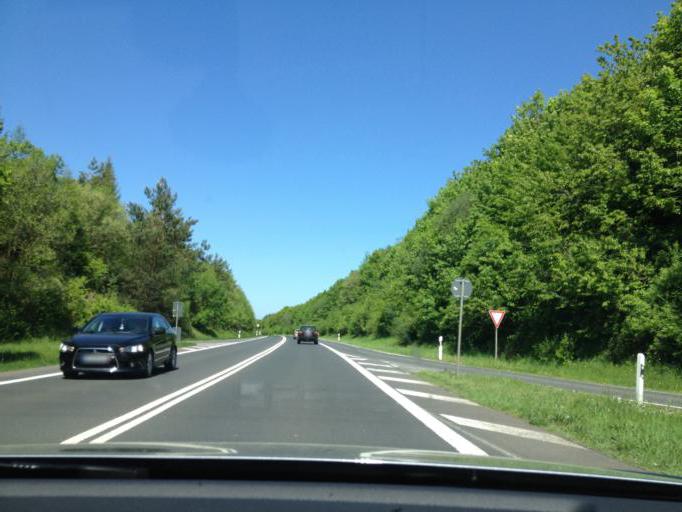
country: DE
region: Rheinland-Pfalz
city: Fliessem
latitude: 50.0158
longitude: 6.5354
